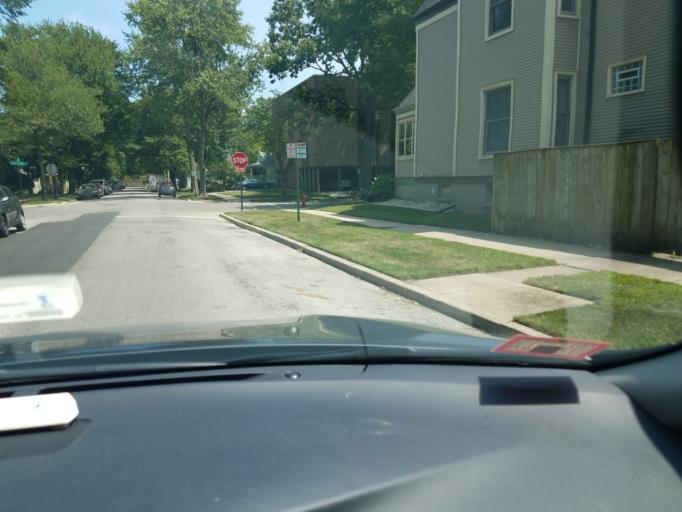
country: US
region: Illinois
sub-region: Cook County
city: Evanston
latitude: 42.0394
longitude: -87.6841
